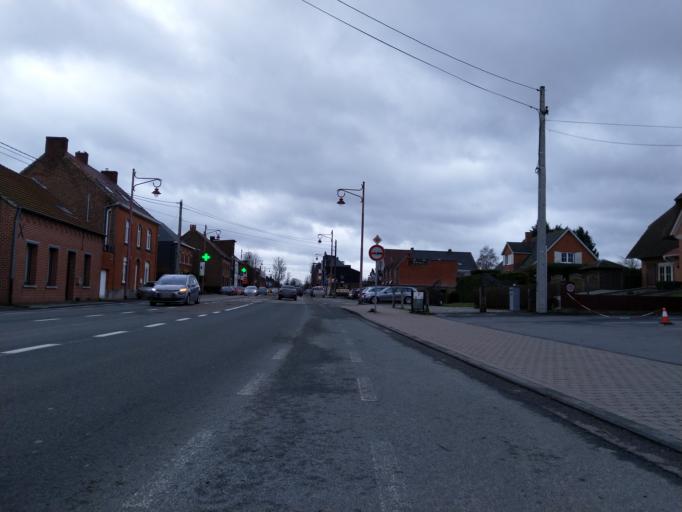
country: BE
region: Wallonia
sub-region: Province du Hainaut
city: Jurbise
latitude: 50.5296
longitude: 3.9123
